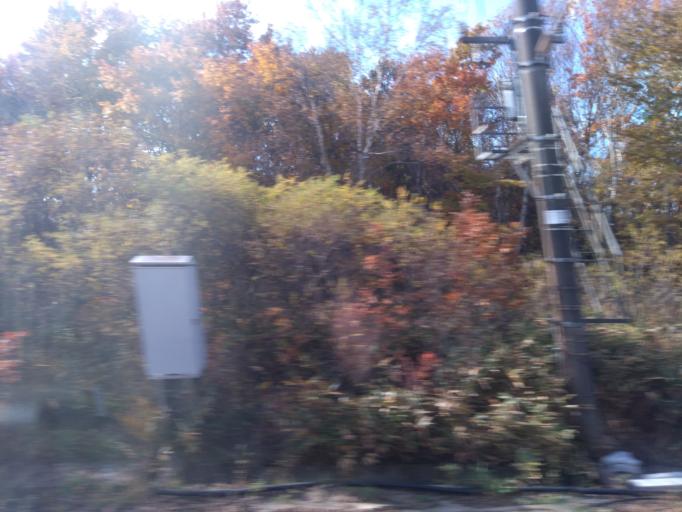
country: JP
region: Hokkaido
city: Kitahiroshima
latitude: 42.9652
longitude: 141.5678
